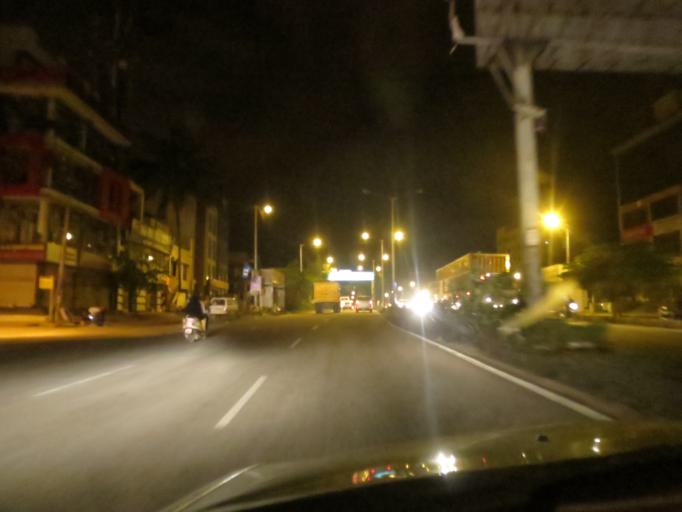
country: IN
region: Karnataka
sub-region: Bangalore Urban
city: Bangalore
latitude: 13.0169
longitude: 77.6606
